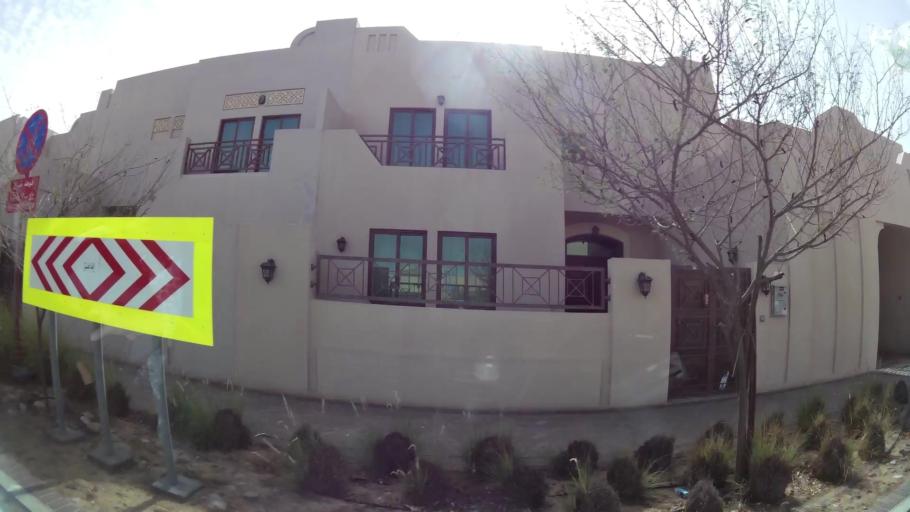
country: AE
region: Abu Dhabi
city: Abu Dhabi
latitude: 24.4073
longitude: 54.5317
